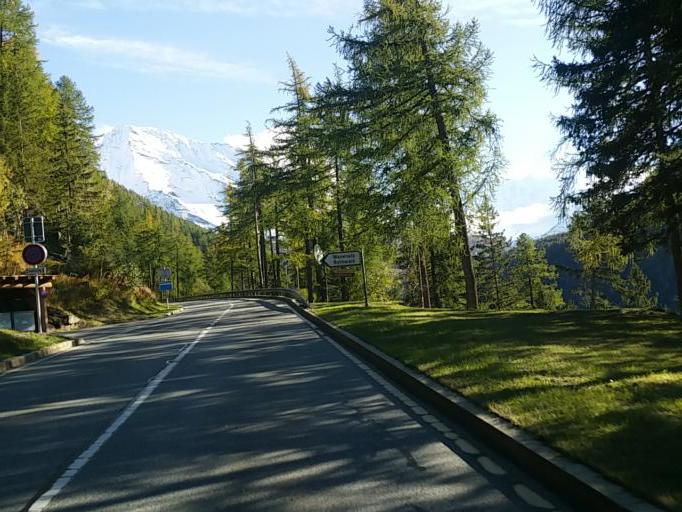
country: CH
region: Valais
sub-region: Brig District
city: Brig
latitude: 46.2789
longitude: 8.0381
